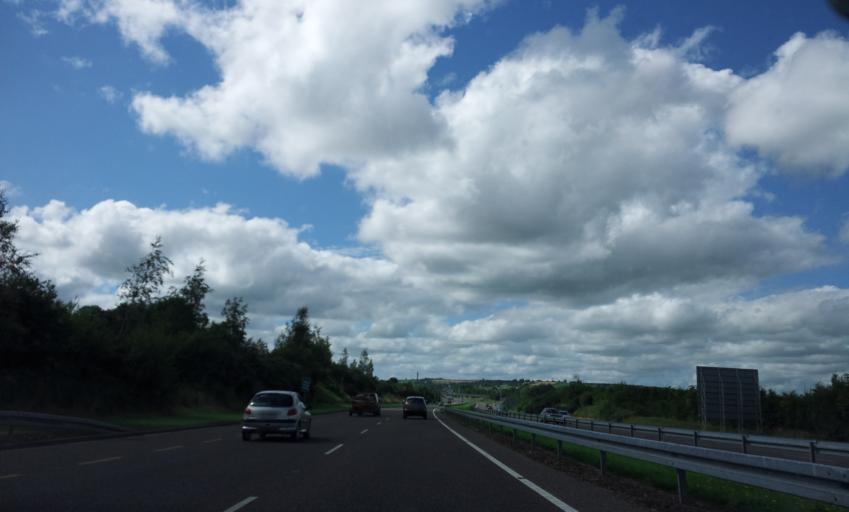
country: IE
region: Munster
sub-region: County Cork
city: Tower
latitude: 51.8741
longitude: -8.6036
